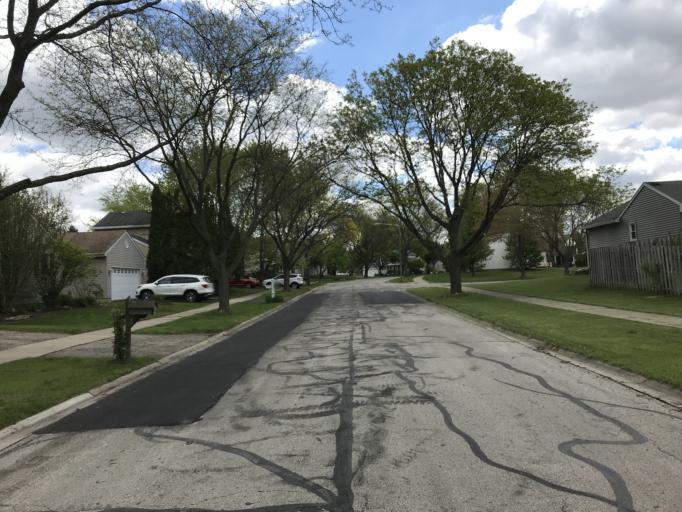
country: US
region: Illinois
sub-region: Will County
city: Bolingbrook
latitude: 41.7394
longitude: -88.1067
